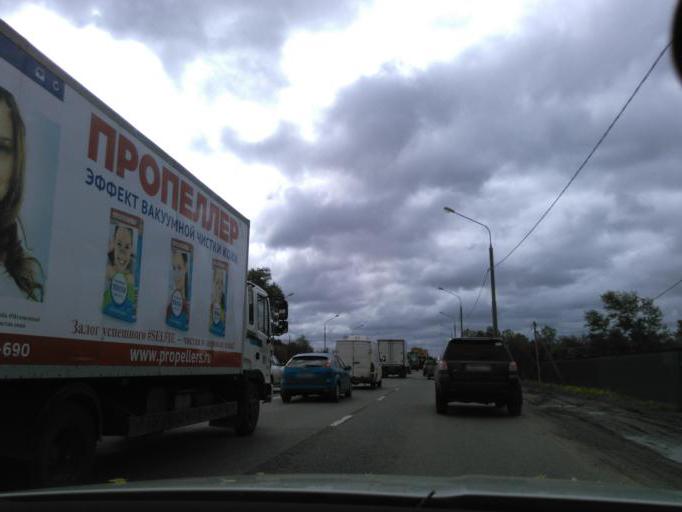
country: RU
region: Moskovskaya
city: Novopodrezkovo
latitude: 55.9378
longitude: 37.3683
